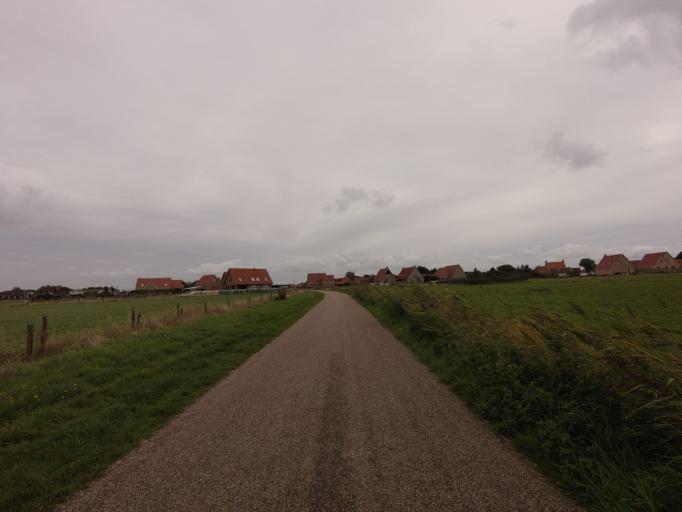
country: NL
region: Friesland
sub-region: Gemeente Ameland
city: Nes
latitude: 53.4517
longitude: 5.7977
